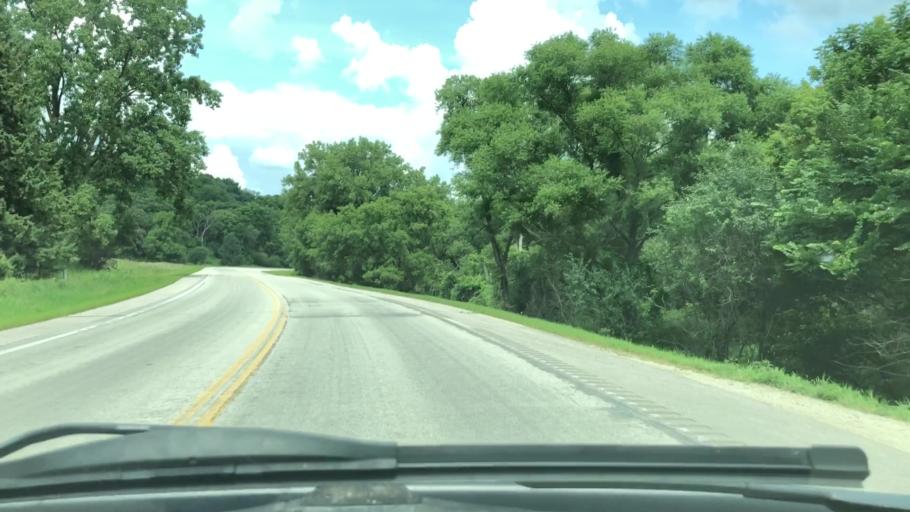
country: US
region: Minnesota
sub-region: Olmsted County
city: Rochester
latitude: 43.9794
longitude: -92.5093
